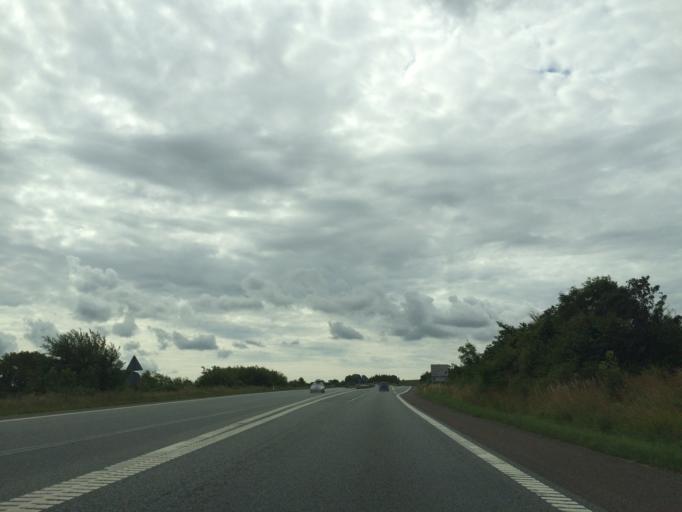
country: DK
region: Central Jutland
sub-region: Syddjurs Kommune
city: Ronde
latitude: 56.3076
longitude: 10.5026
